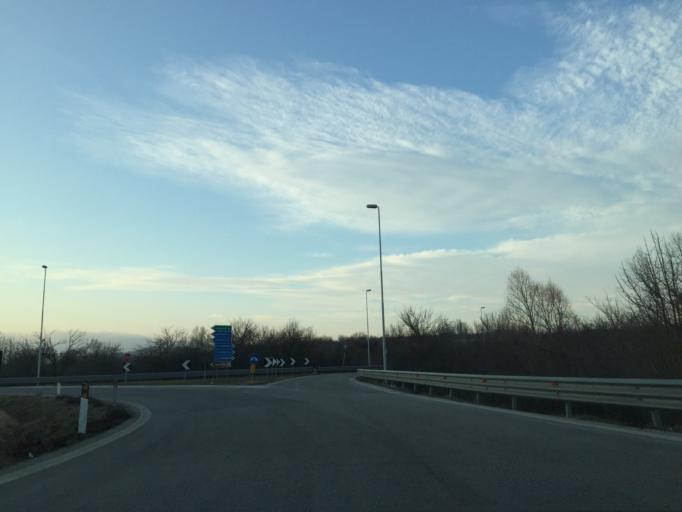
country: IT
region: Molise
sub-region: Provincia di Campobasso
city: Guardiaregia
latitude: 41.4633
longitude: 14.5589
